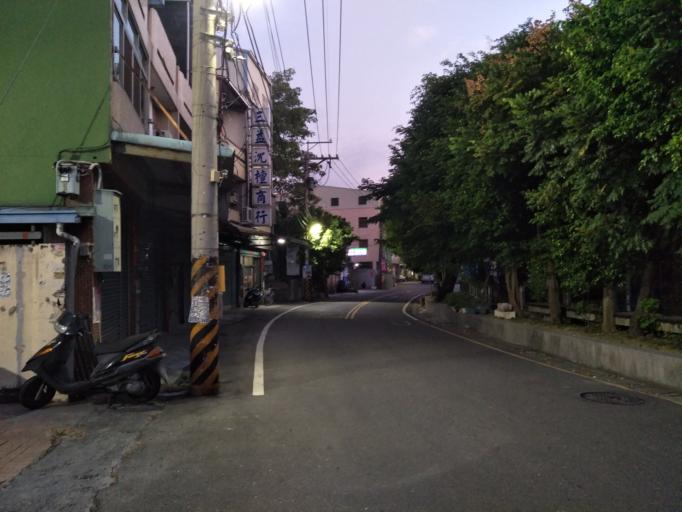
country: TW
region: Taiwan
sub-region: Changhua
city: Chang-hua
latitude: 23.9474
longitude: 120.5263
